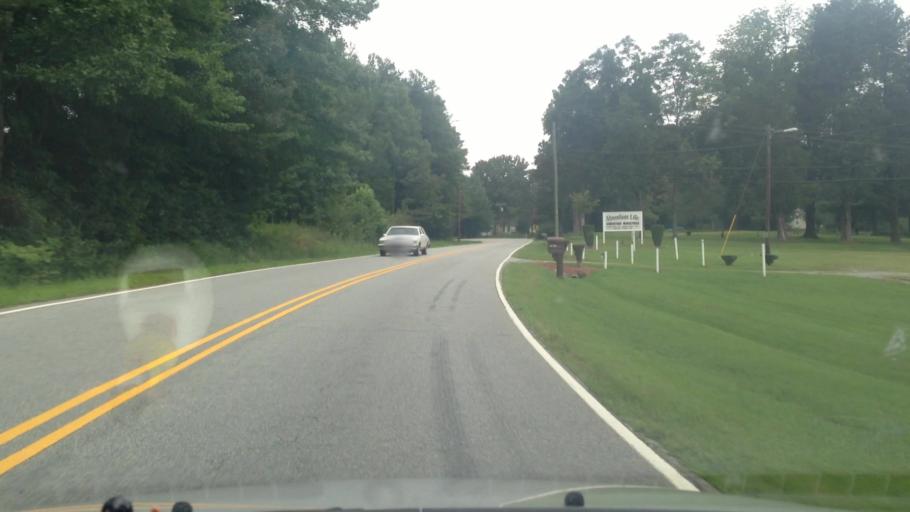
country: US
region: North Carolina
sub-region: Forsyth County
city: Walkertown
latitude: 36.2118
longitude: -80.1681
